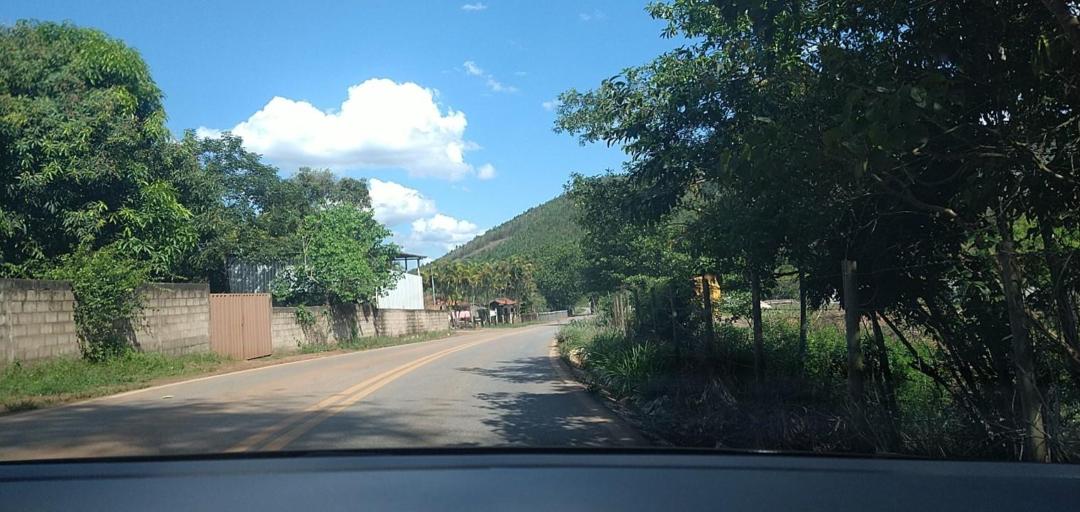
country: BR
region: Minas Gerais
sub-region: Rio Piracicaba
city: Rio Piracicaba
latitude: -19.9508
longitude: -43.1715
